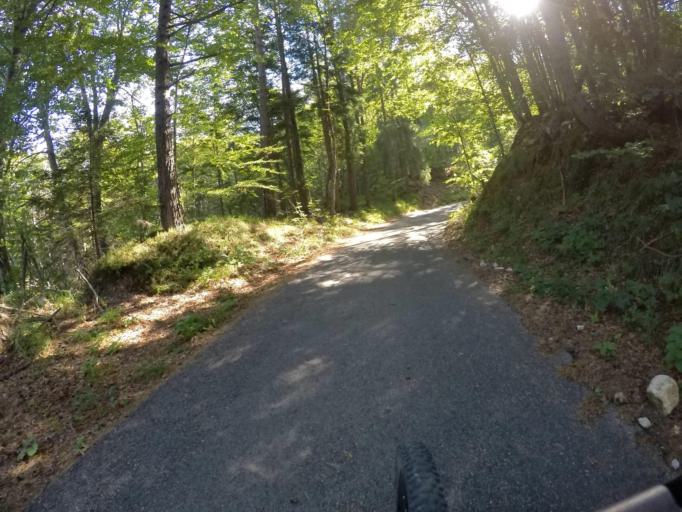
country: IT
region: Friuli Venezia Giulia
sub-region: Provincia di Udine
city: Zuglio
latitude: 46.4410
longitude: 13.0872
